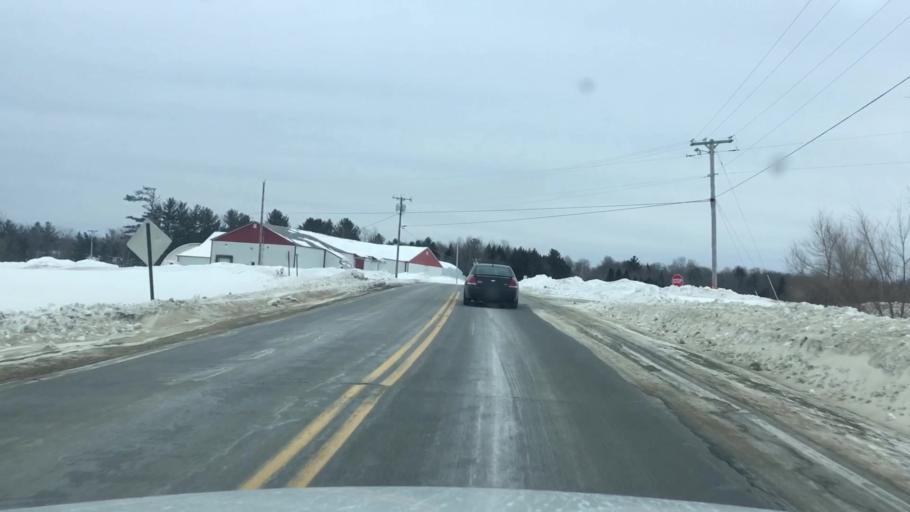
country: US
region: Maine
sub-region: Penobscot County
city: Garland
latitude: 44.9894
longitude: -69.0877
